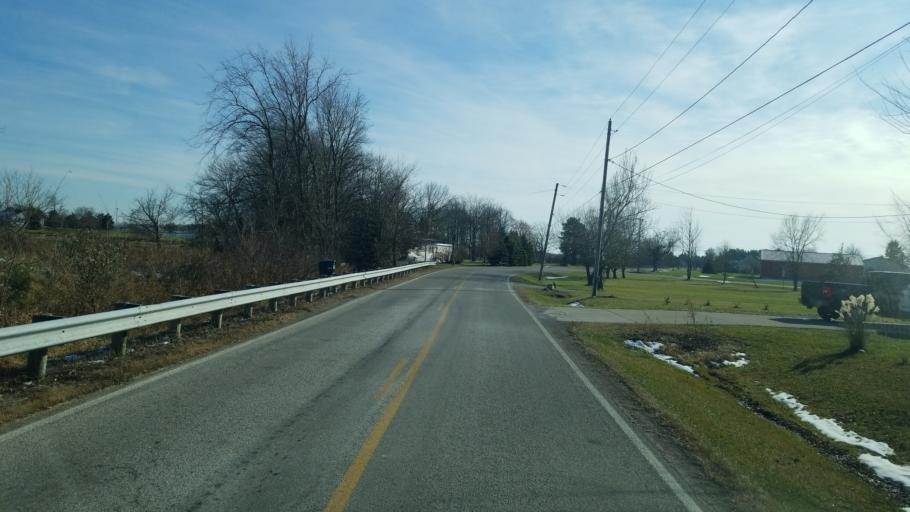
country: US
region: Ohio
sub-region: Lorain County
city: Camden
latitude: 41.1788
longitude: -82.3506
